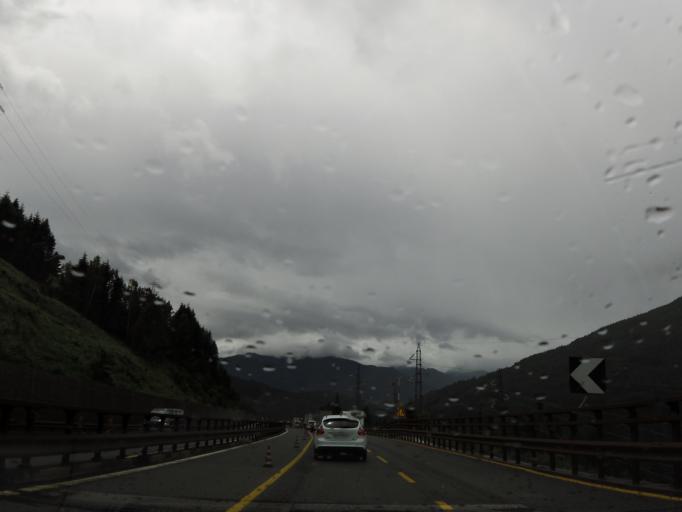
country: IT
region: Trentino-Alto Adige
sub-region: Bolzano
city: Colle Isarco
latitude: 46.9409
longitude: 11.4490
